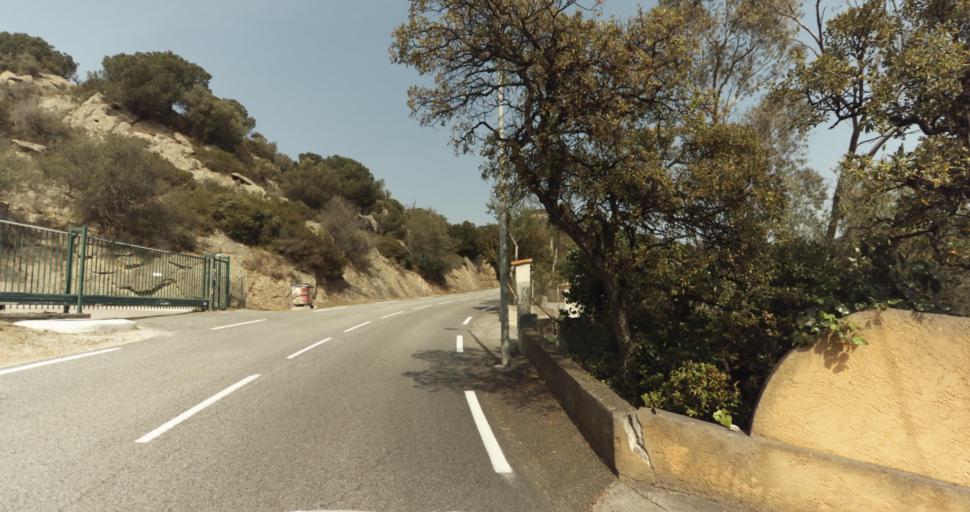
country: FR
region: Provence-Alpes-Cote d'Azur
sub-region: Departement du Var
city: Bormes-les-Mimosas
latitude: 43.1540
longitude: 6.3453
